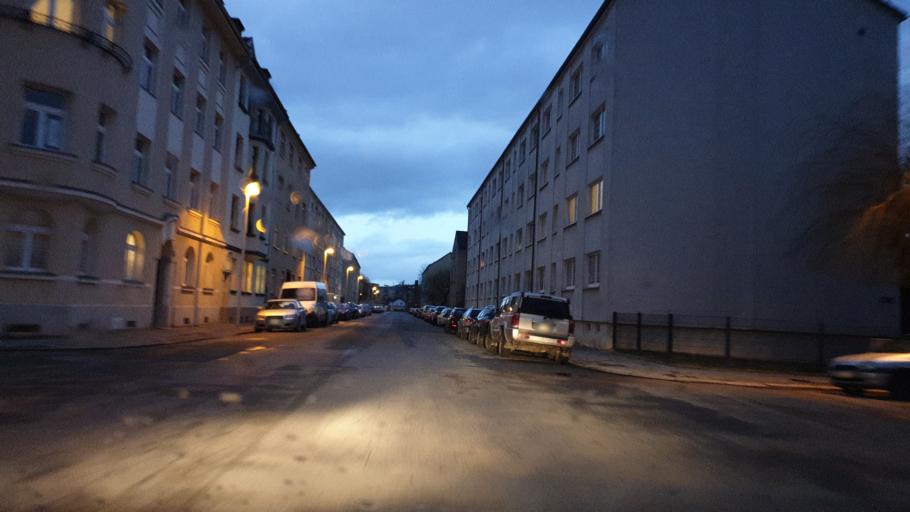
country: DE
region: Thuringia
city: Gera
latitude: 50.8635
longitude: 12.0712
